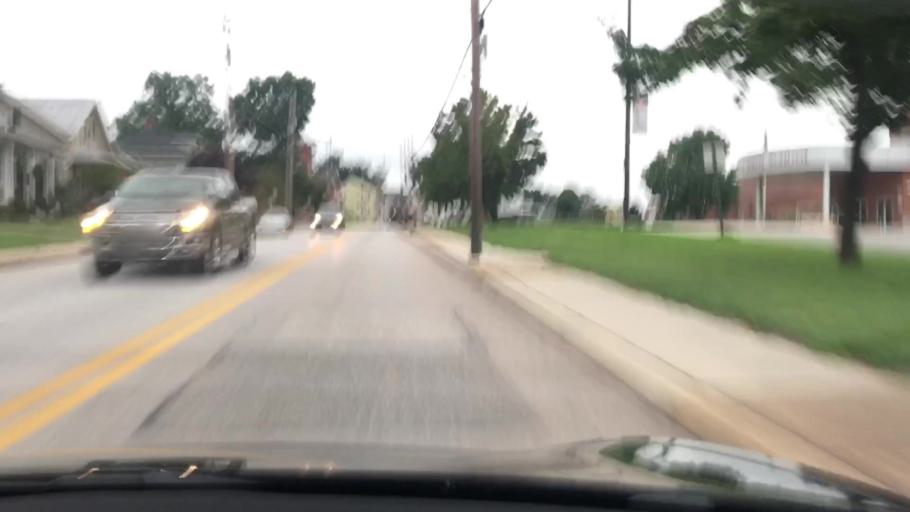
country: US
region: Pennsylvania
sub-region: York County
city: Dover
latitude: 39.9990
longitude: -76.8534
